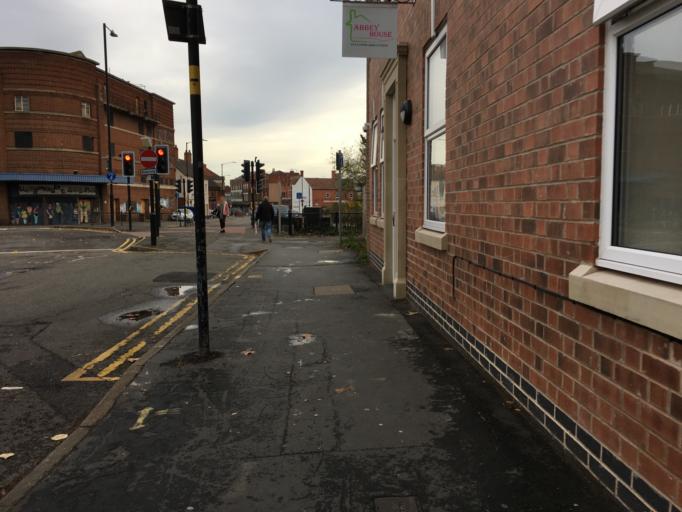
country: GB
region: England
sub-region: Warwickshire
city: Nuneaton
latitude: 52.5249
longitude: -1.4725
